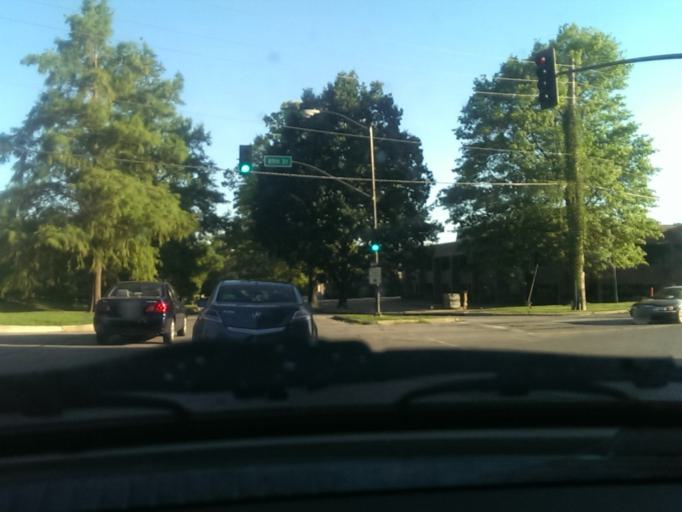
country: US
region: Kansas
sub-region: Johnson County
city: Leawood
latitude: 38.9673
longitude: -94.6052
